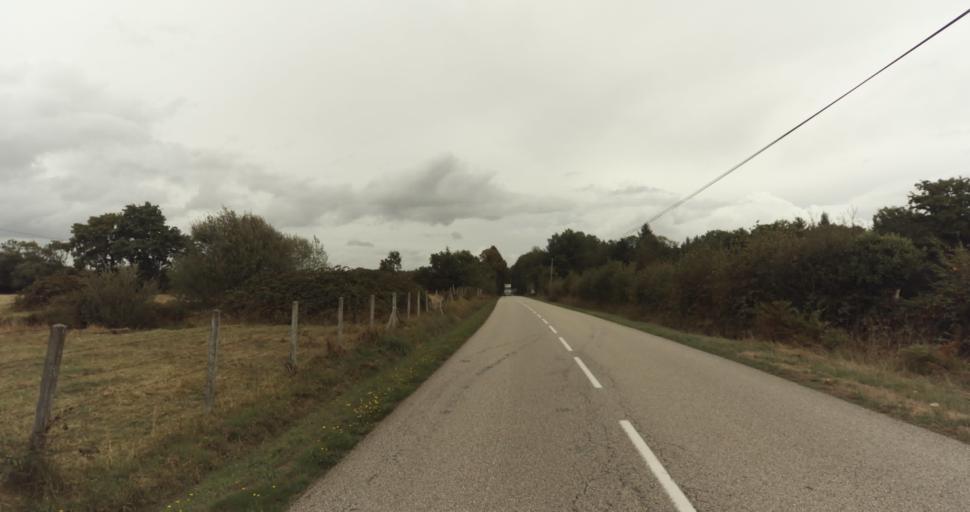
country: FR
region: Lower Normandy
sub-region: Departement de l'Orne
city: Gace
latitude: 48.7948
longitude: 0.3537
